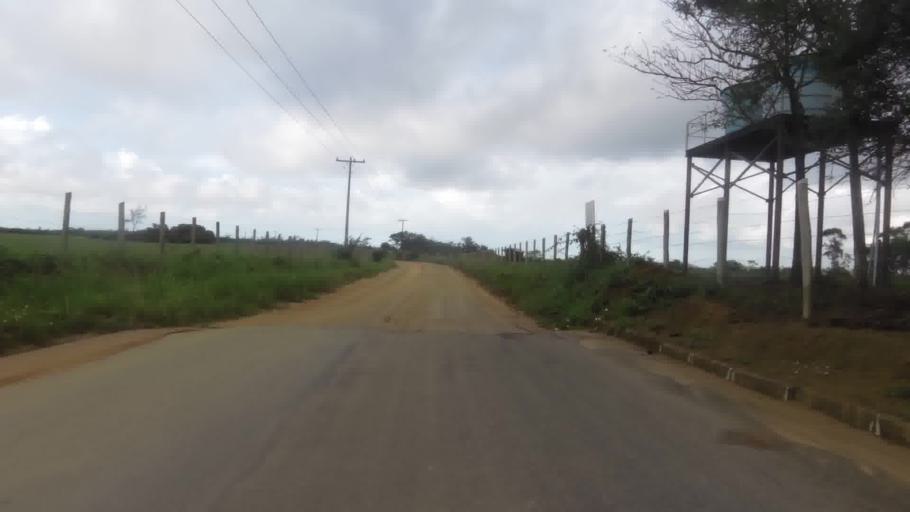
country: BR
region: Espirito Santo
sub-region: Piuma
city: Piuma
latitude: -20.7732
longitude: -40.6305
